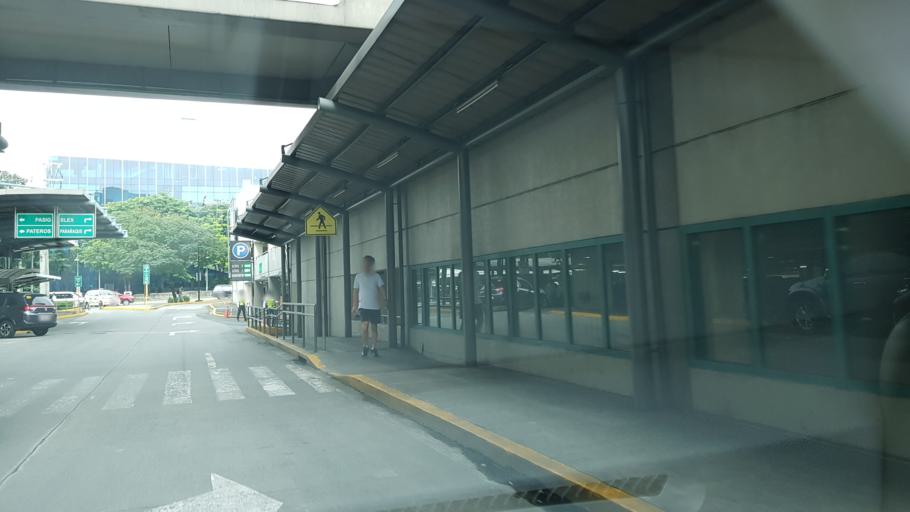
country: PH
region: Calabarzon
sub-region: Province of Rizal
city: Pateros
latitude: 14.5507
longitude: 121.0570
